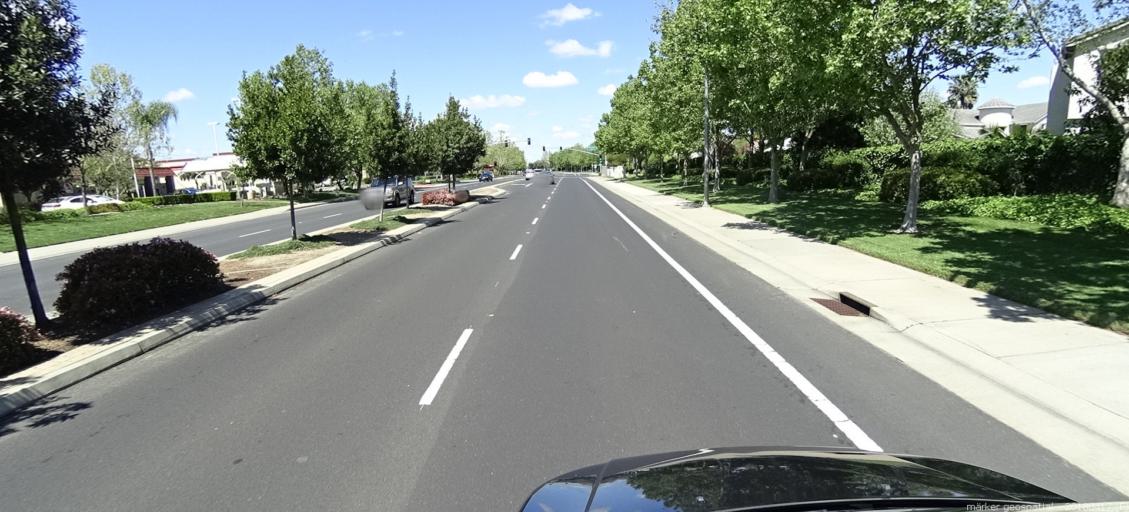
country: US
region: California
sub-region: Sacramento County
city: Laguna
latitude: 38.4241
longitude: -121.4806
